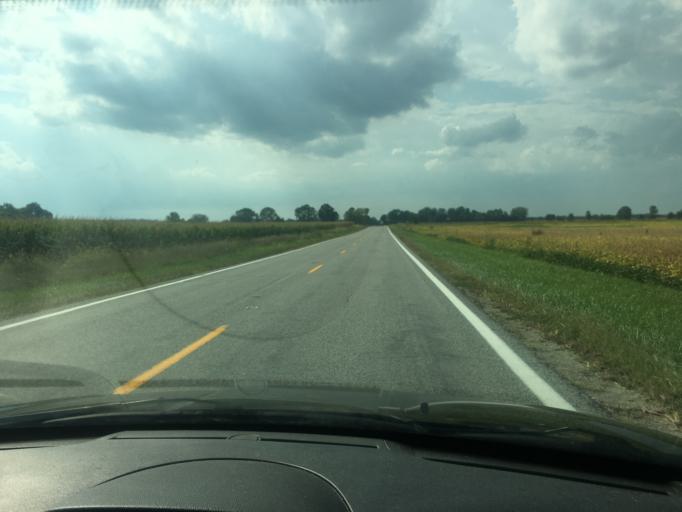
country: US
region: Ohio
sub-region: Champaign County
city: Urbana
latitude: 40.1558
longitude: -83.7527
